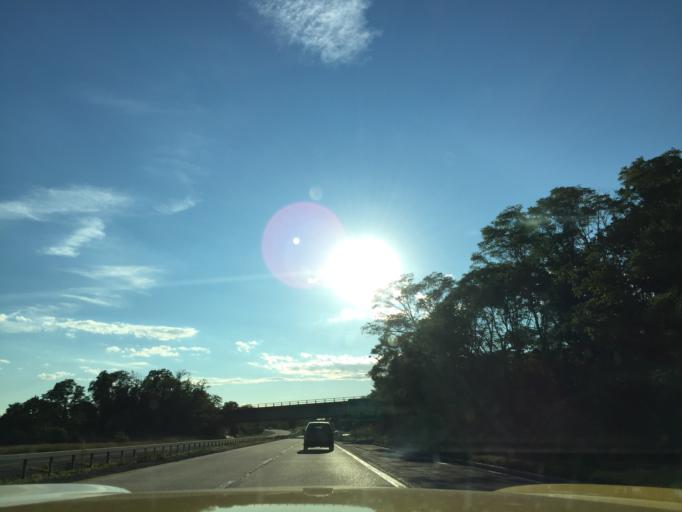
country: US
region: New York
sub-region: Suffolk County
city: Calverton
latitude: 40.9227
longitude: -72.7175
